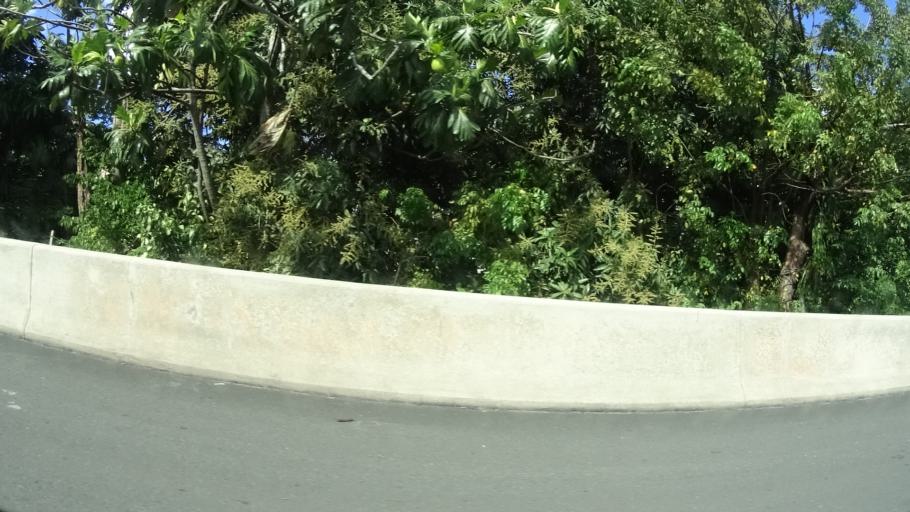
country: PR
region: Rio Grande
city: Palmer
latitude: 18.3712
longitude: -65.7740
